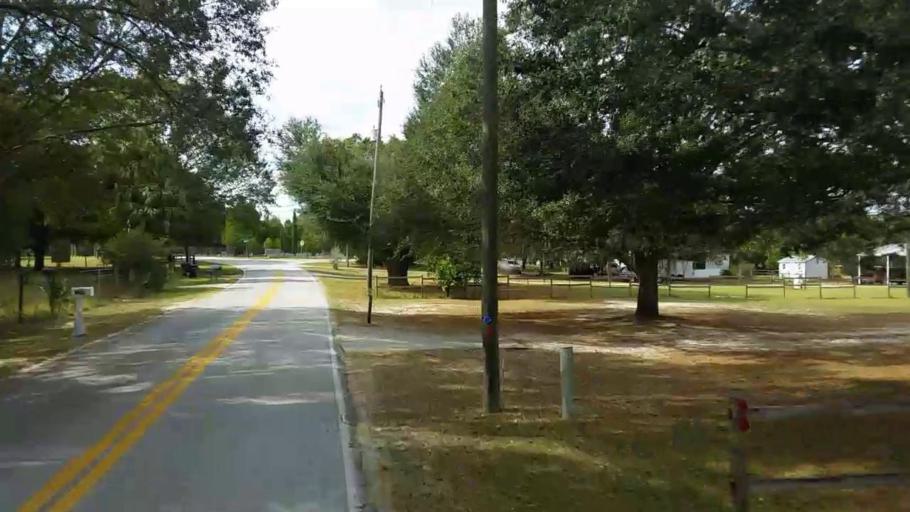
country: US
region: Florida
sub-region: Polk County
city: Polk City
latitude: 28.3268
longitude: -81.8416
